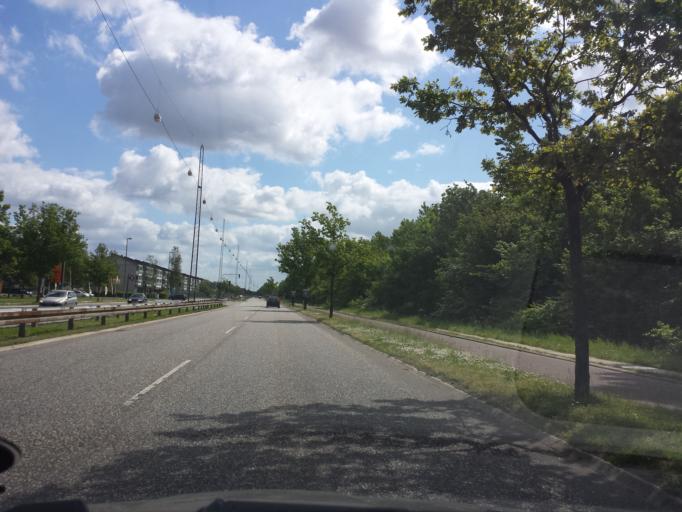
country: DK
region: Capital Region
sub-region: Ballerup Kommune
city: Ballerup
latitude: 55.7217
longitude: 12.3826
